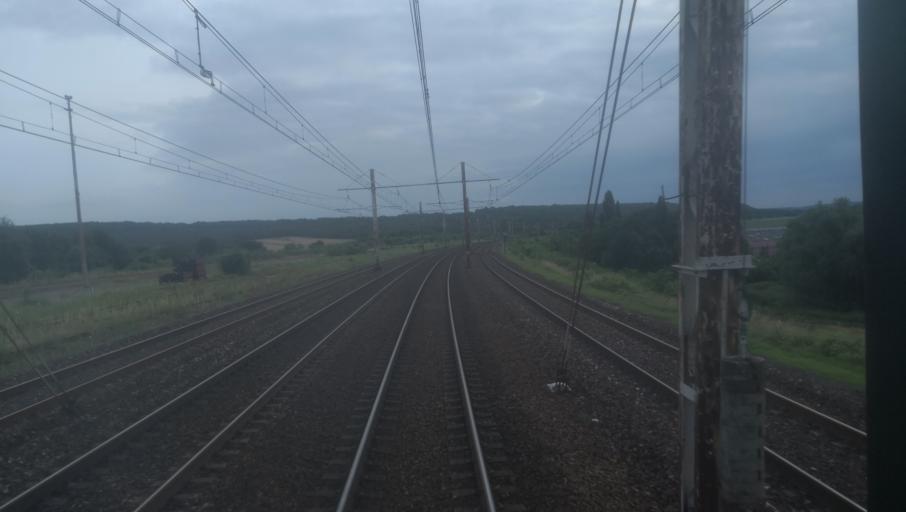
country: FR
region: Ile-de-France
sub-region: Departement de l'Essonne
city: Morigny-Champigny
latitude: 48.4534
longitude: 2.1678
